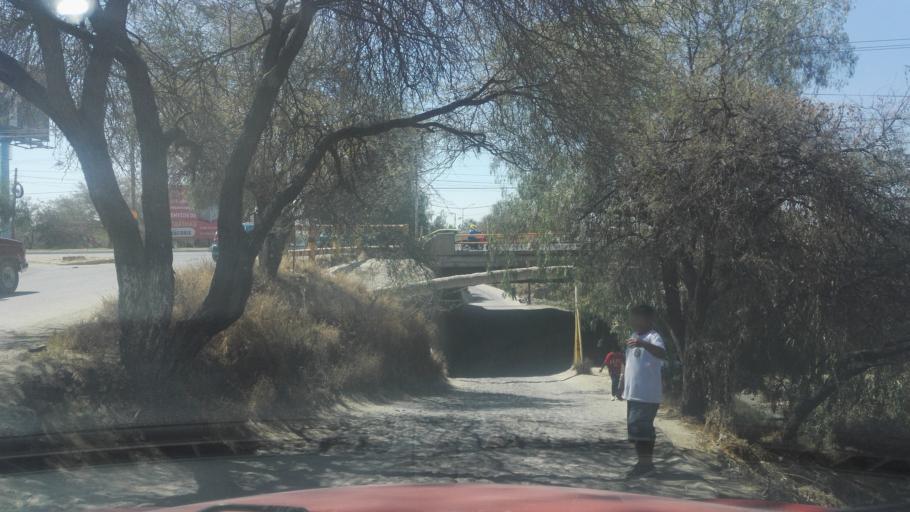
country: MX
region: Guanajuato
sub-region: Leon
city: Fraccionamiento Paraiso Real
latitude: 21.0744
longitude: -101.6002
